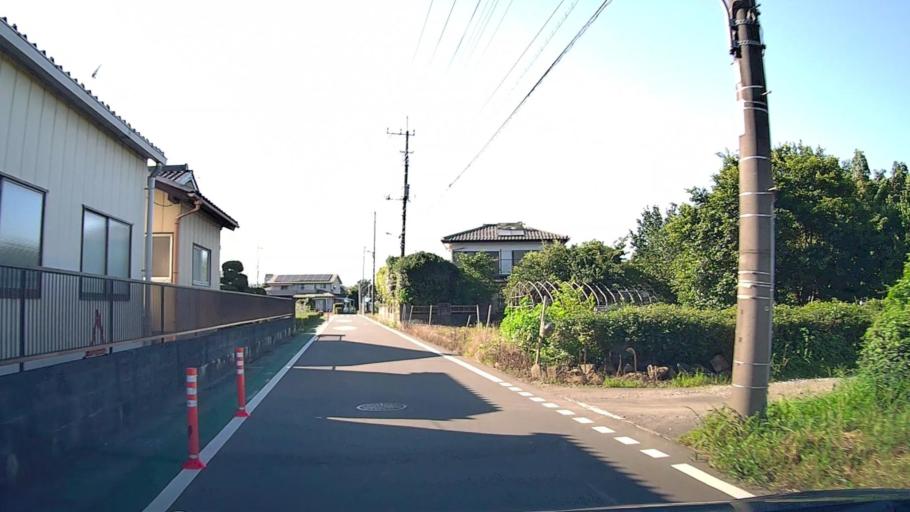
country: JP
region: Tokyo
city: Fussa
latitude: 35.7866
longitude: 139.3623
